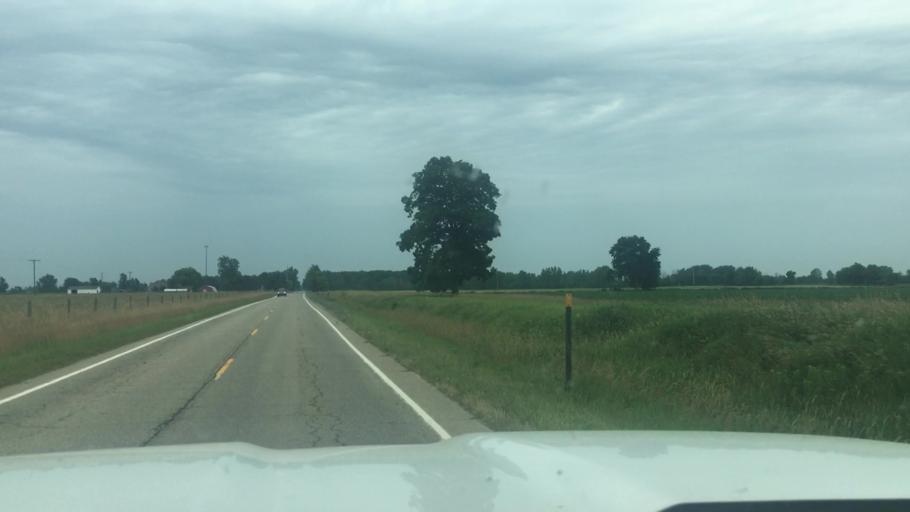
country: US
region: Michigan
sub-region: Clinton County
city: Saint Johns
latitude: 43.0146
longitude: -84.4841
